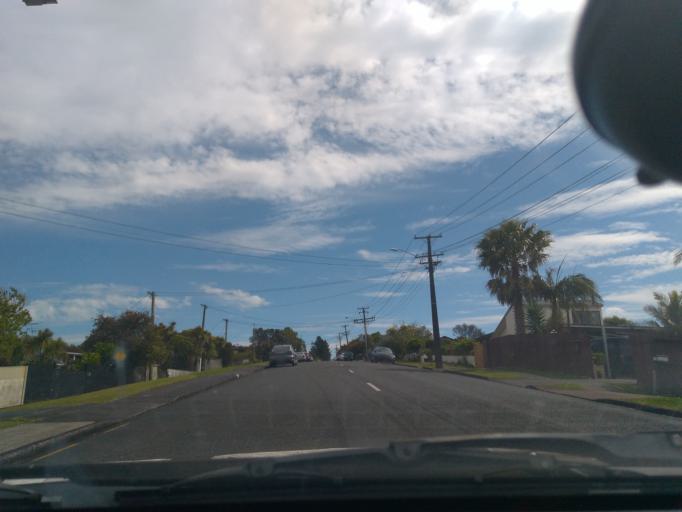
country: NZ
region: Auckland
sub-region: Auckland
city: Titirangi
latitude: -36.9327
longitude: 174.6740
